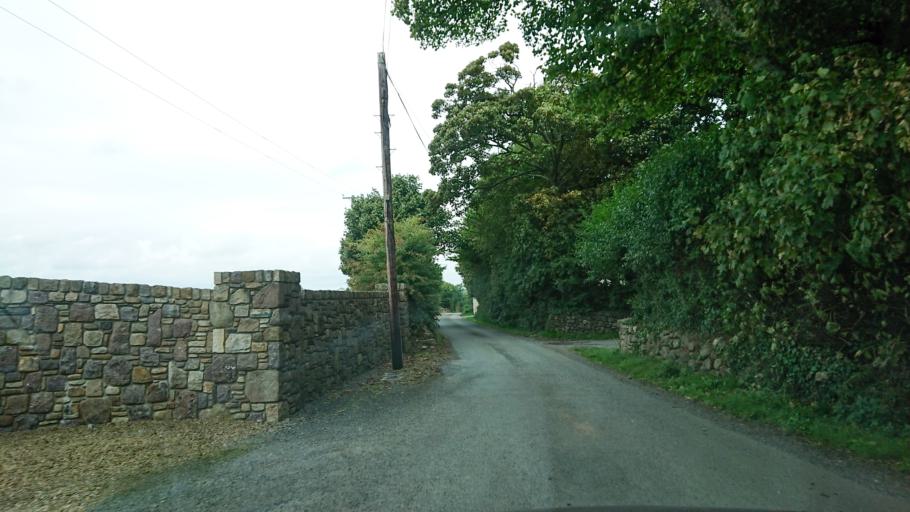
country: IE
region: Munster
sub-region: Waterford
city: Waterford
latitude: 52.2139
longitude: -7.0426
